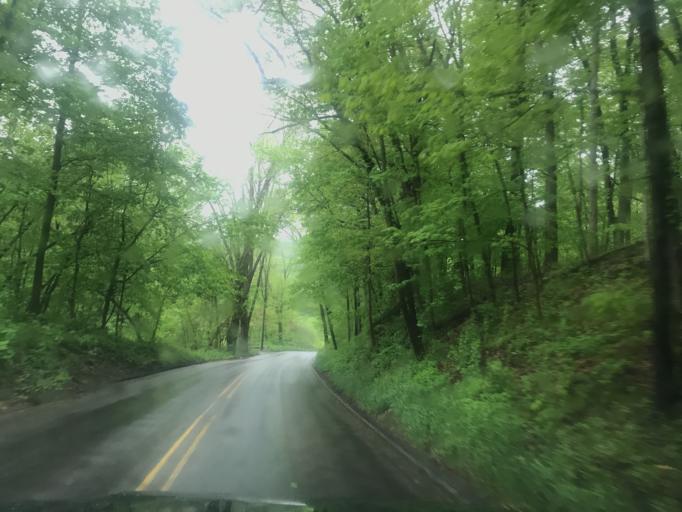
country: US
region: Connecticut
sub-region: Fairfield County
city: Bethel
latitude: 41.3105
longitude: -73.3608
